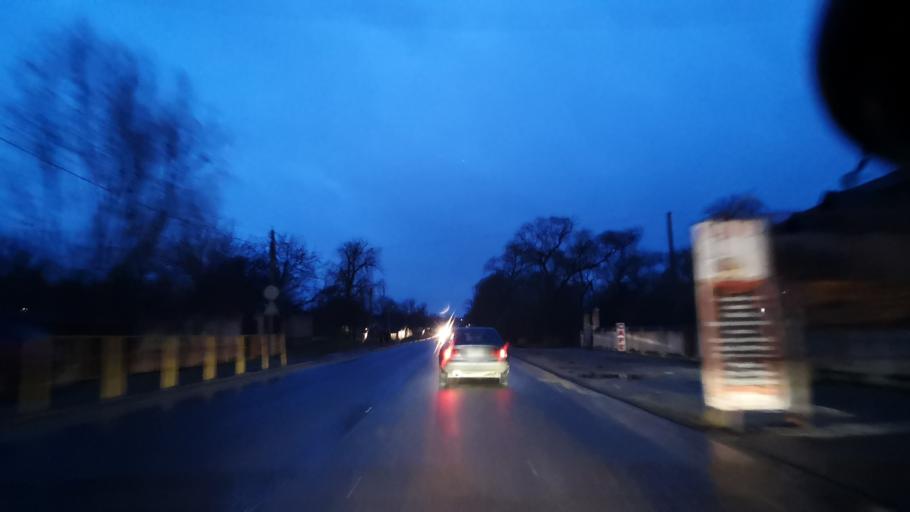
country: MD
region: Orhei
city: Orhei
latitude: 47.4249
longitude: 28.8044
